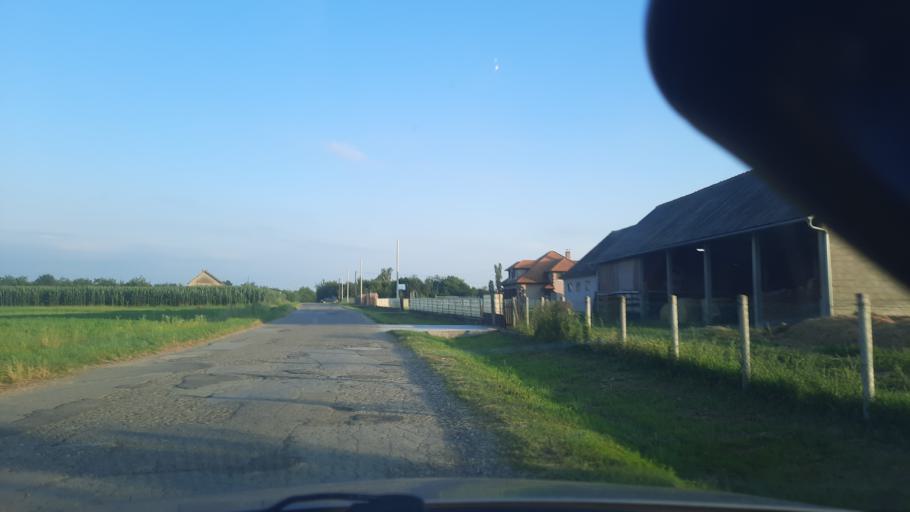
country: RS
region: Central Serbia
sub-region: Macvanski Okrug
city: Vladimirci
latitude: 44.6330
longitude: 19.8427
